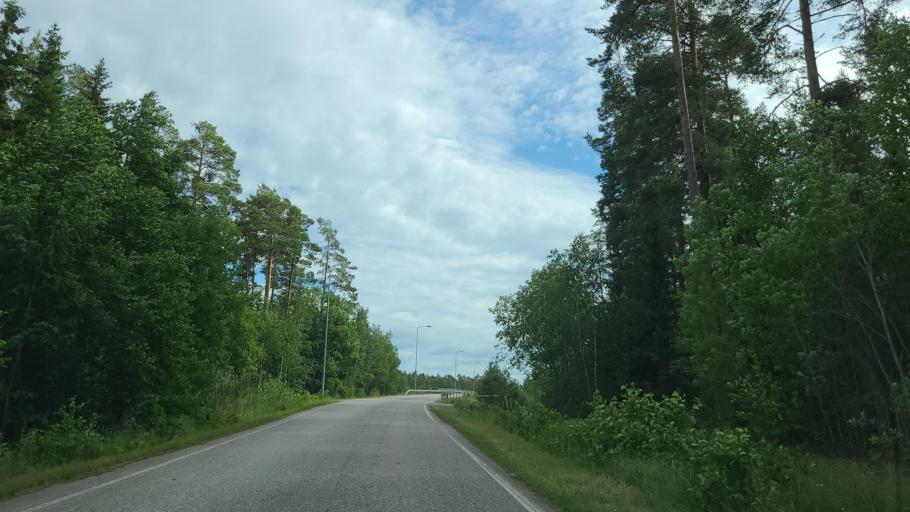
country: FI
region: Varsinais-Suomi
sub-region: Turku
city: Rymaettylae
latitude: 60.3395
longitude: 21.9785
